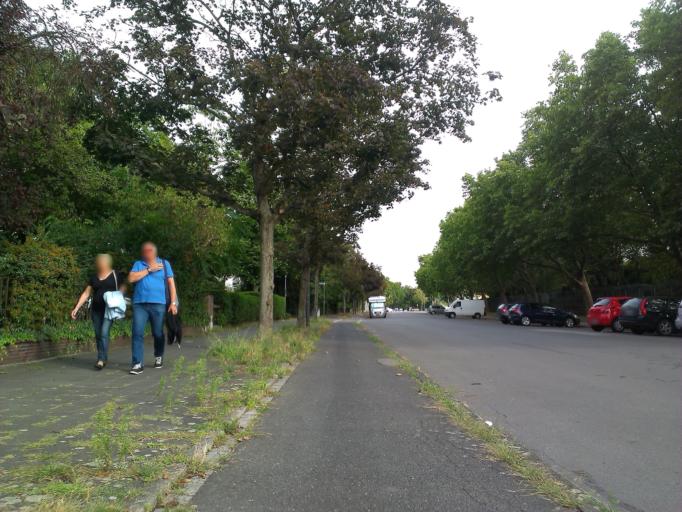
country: DE
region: Rheinland-Pfalz
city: Ludwigshafen am Rhein
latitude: 49.4698
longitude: 8.4420
